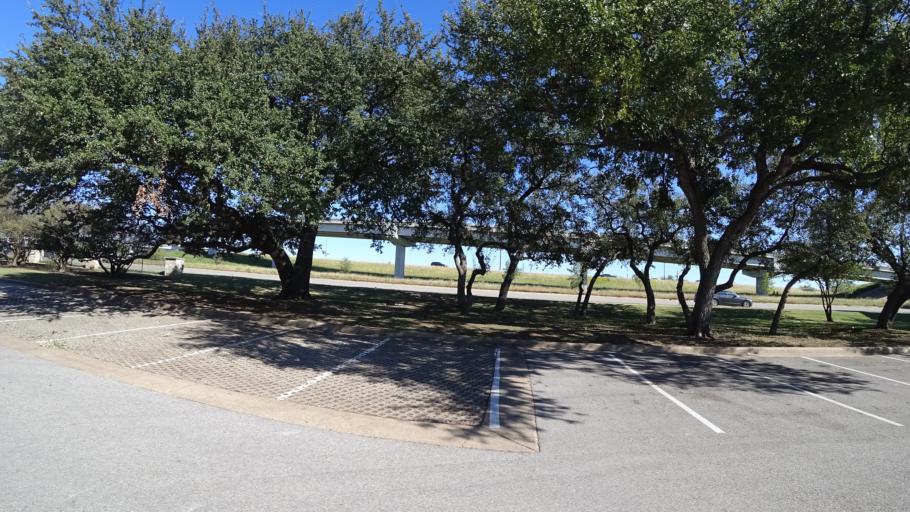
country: US
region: Texas
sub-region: Travis County
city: Rollingwood
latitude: 30.2342
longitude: -97.8266
